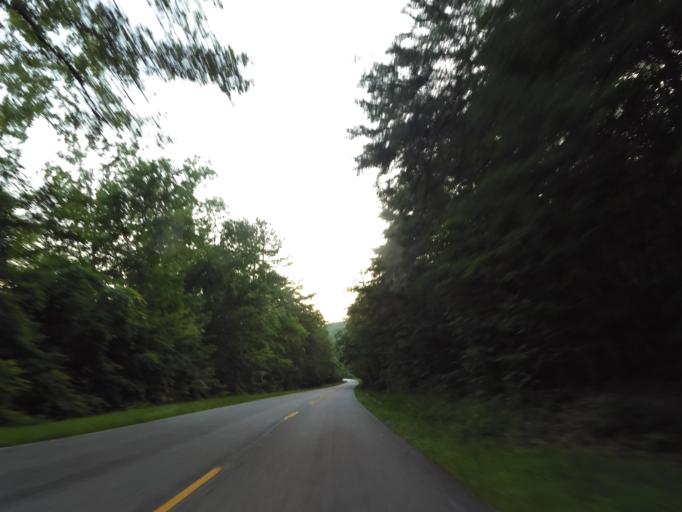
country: US
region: Tennessee
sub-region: Blount County
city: Maryville
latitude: 35.6136
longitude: -83.9702
